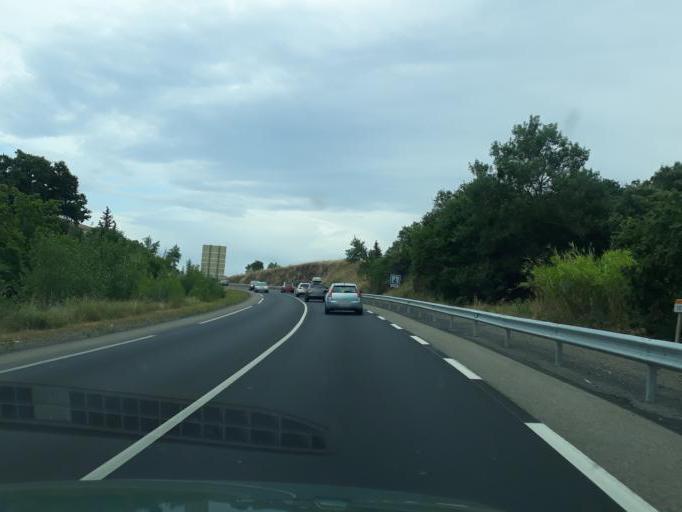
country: FR
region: Languedoc-Roussillon
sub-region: Departement de l'Herault
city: Saint-Thibery
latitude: 43.3909
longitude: 3.4136
